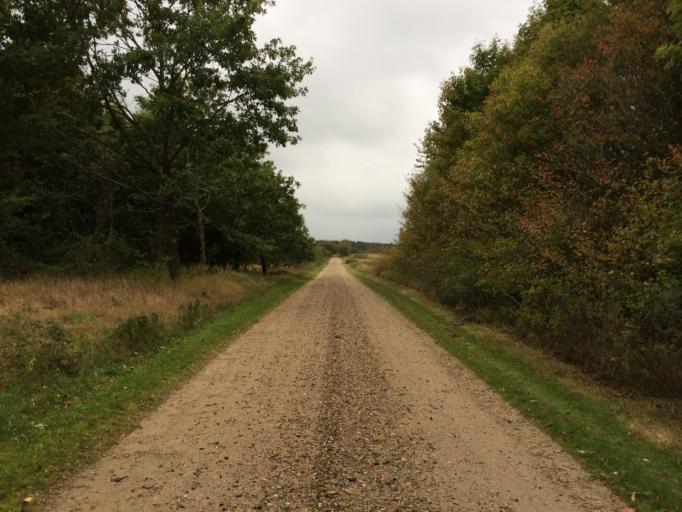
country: DK
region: Central Jutland
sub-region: Holstebro Kommune
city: Ulfborg
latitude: 56.2496
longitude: 8.4166
